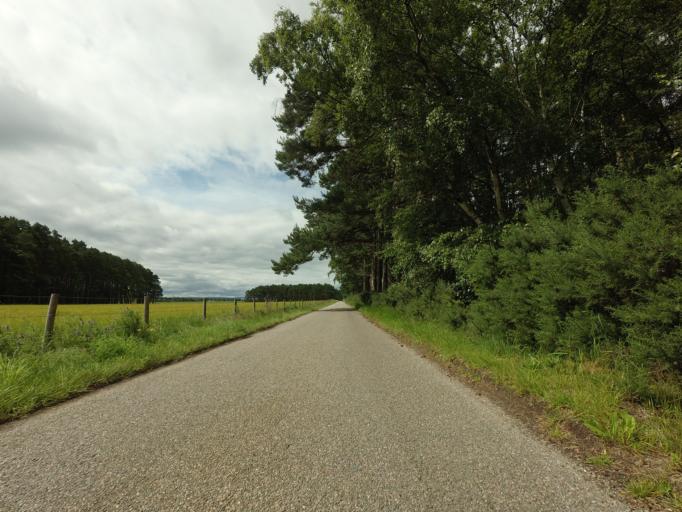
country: GB
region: Scotland
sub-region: Moray
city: Kinloss
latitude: 57.6304
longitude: -3.5844
